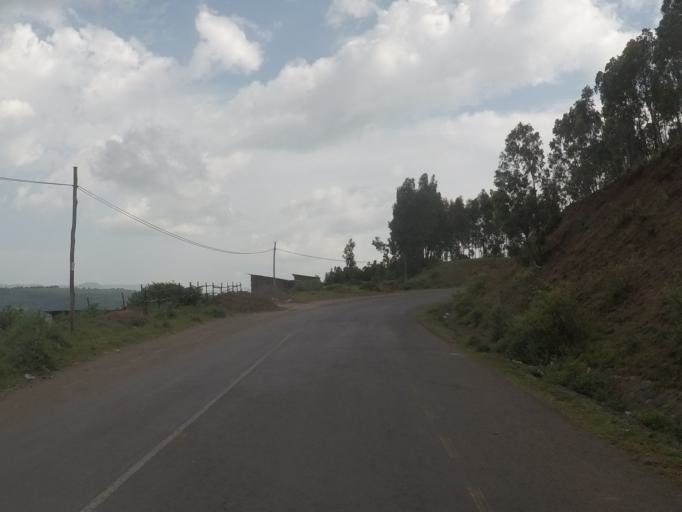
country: ET
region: Amhara
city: Gondar
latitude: 12.6357
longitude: 37.4724
